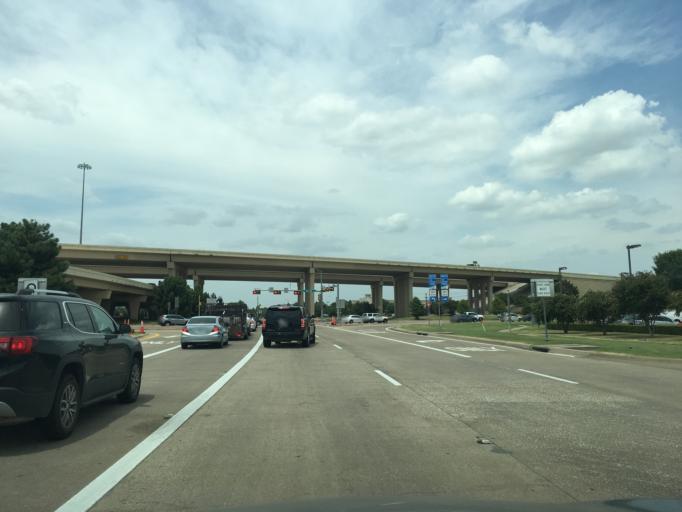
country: US
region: Texas
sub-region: Collin County
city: Frisco
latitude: 33.0958
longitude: -96.8052
